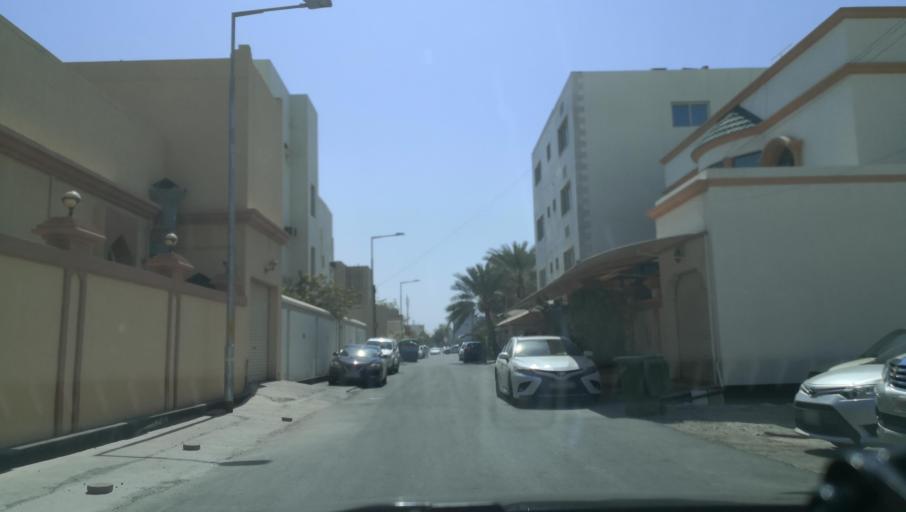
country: BH
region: Muharraq
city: Al Hadd
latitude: 26.2517
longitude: 50.6484
